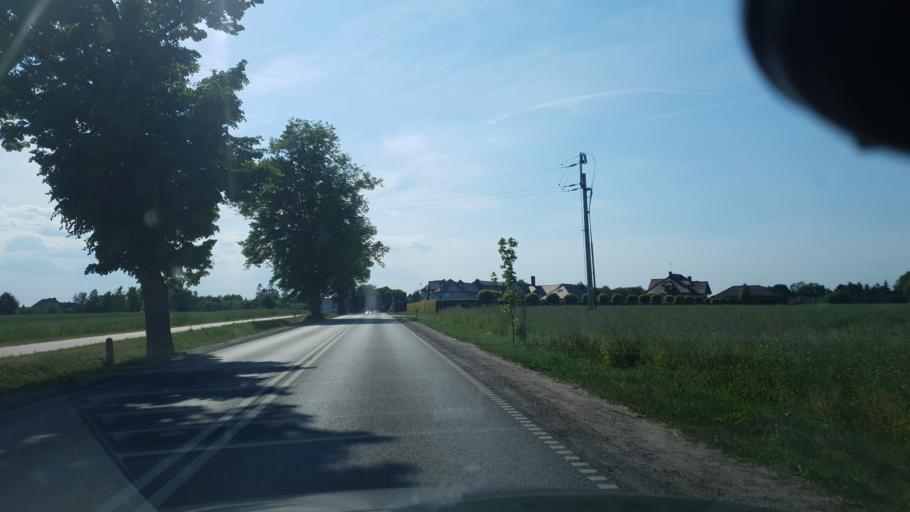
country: PL
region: Pomeranian Voivodeship
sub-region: Powiat kartuski
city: Chwaszczyno
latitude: 54.4426
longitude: 18.4285
